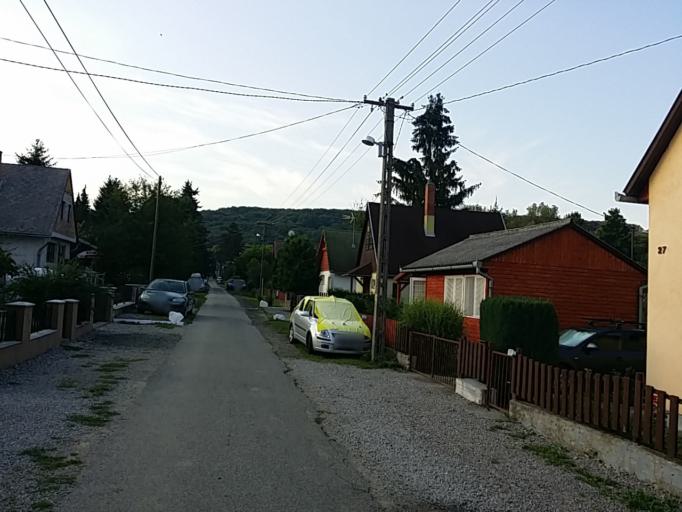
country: HU
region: Baranya
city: Sasd
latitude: 46.1418
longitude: 18.1159
